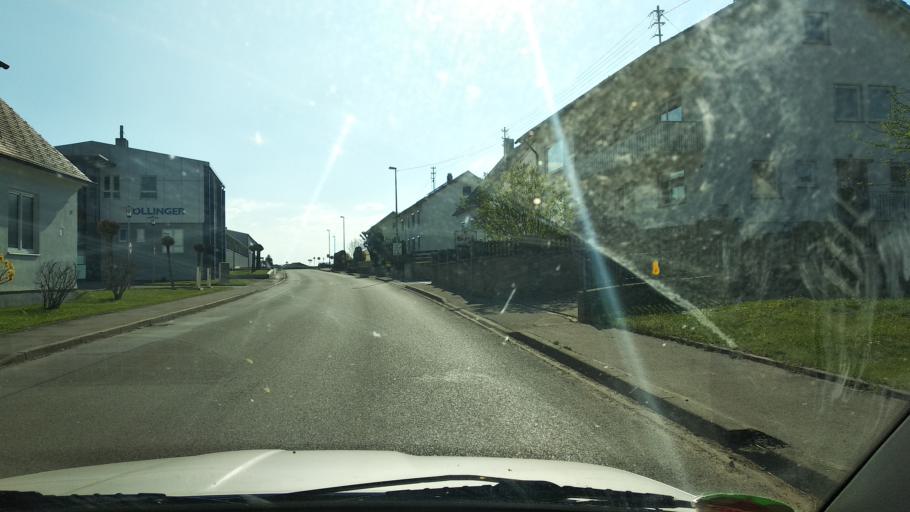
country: DE
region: Bavaria
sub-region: Swabia
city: Hawangen
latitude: 47.9701
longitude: 10.2607
